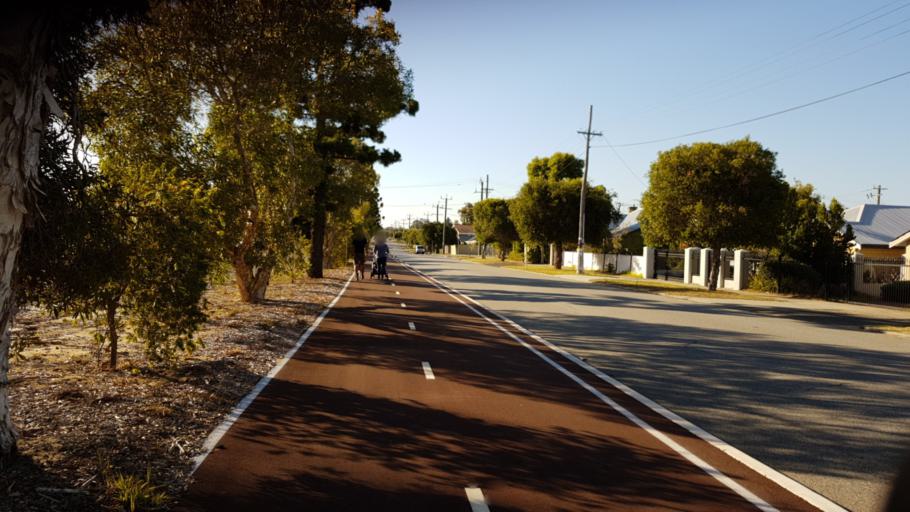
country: AU
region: Western Australia
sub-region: Victoria Park
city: Victoria Park
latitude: -31.9831
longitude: 115.9136
